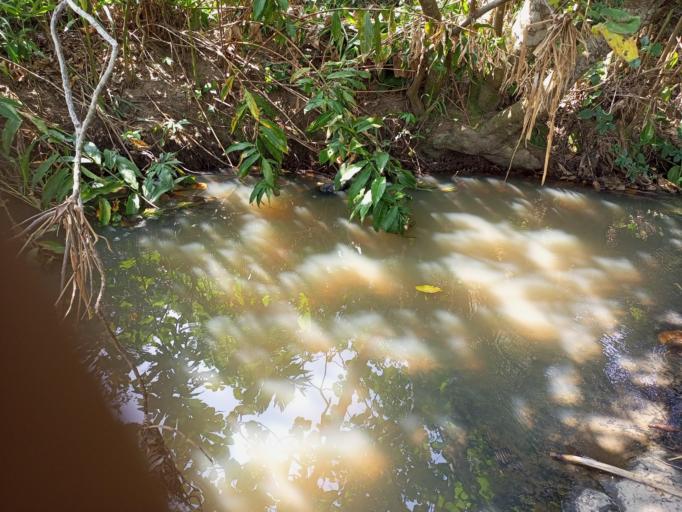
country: CD
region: Eastern Province
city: Bunia
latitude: 1.5385
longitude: 30.2934
